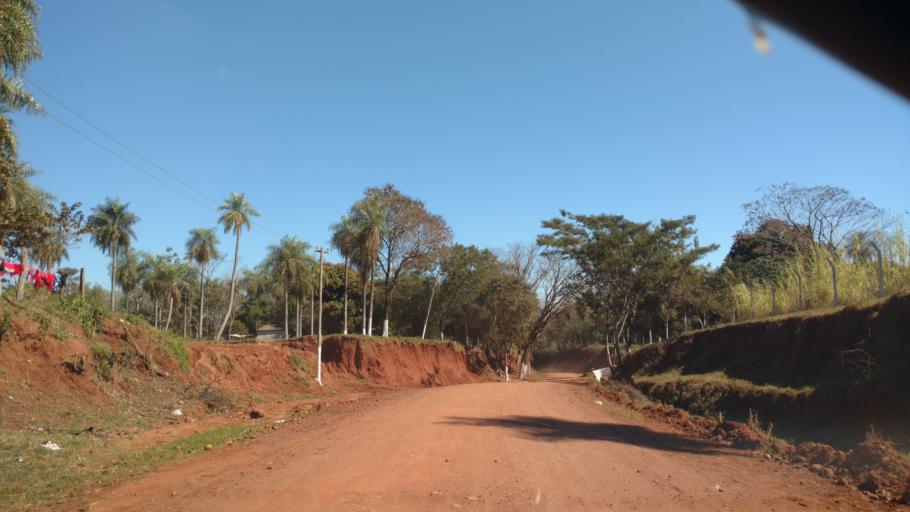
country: PY
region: Paraguari
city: Yaguaron
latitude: -25.5644
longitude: -57.3026
